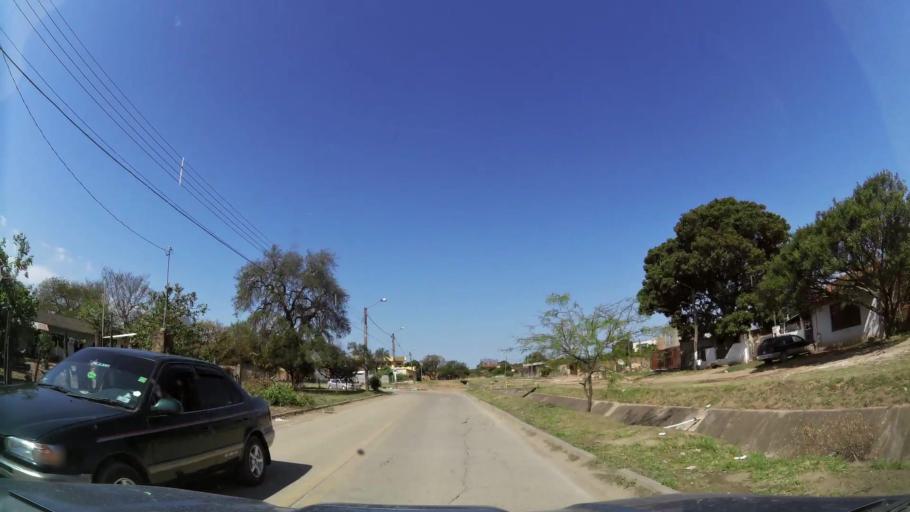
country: BO
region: Santa Cruz
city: Santa Cruz de la Sierra
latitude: -17.7595
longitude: -63.1192
